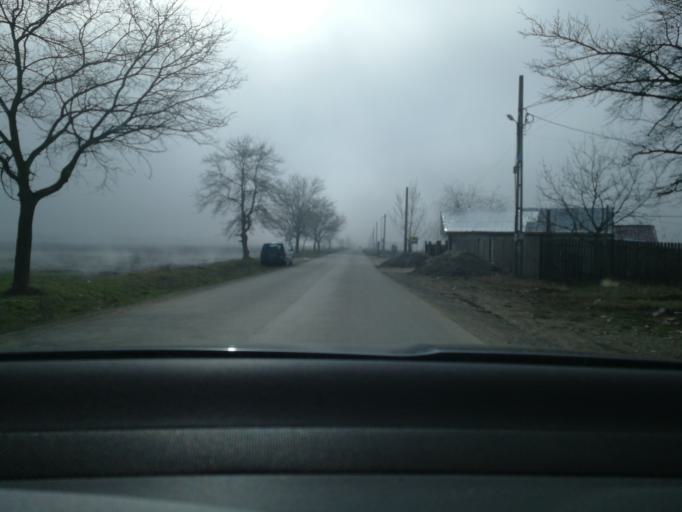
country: RO
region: Prahova
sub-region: Comuna Magureni
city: Lunca Prahovei
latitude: 45.0312
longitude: 25.7672
